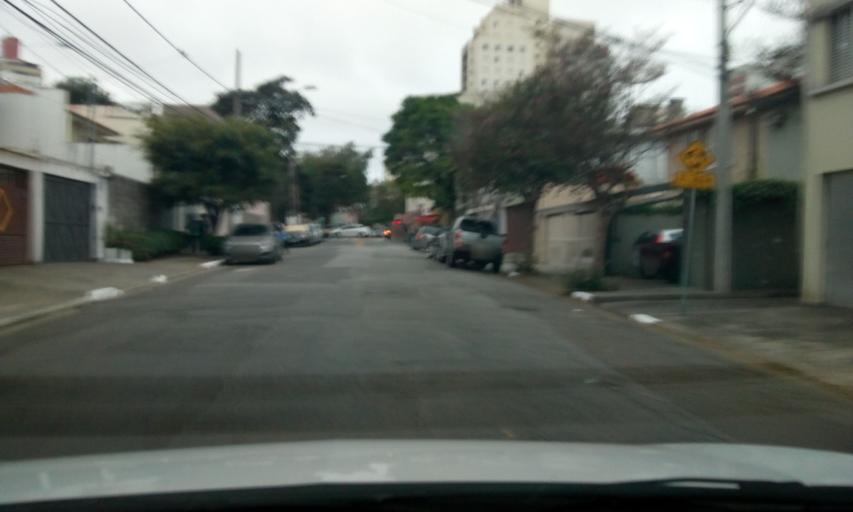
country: BR
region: Sao Paulo
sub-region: Sao Paulo
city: Sao Paulo
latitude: -23.5909
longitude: -46.6441
